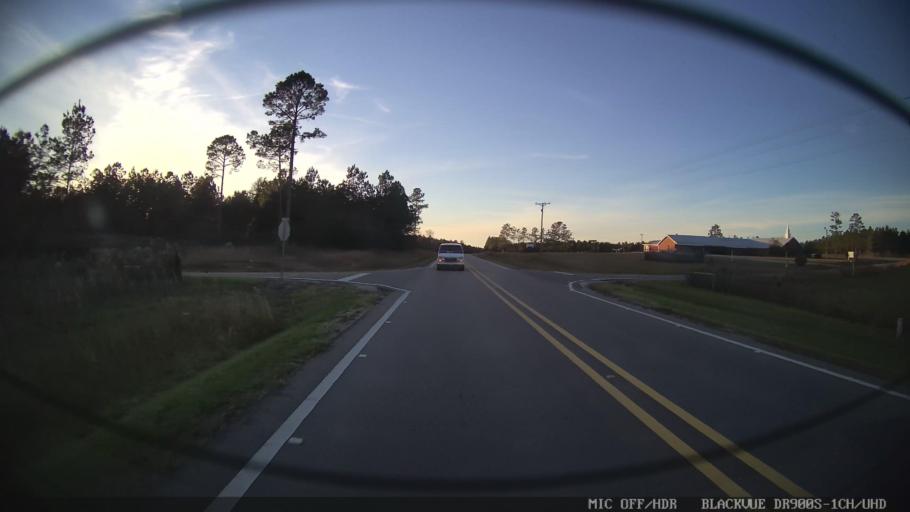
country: US
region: Mississippi
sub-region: Lamar County
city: Lumberton
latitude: 30.9924
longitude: -89.2816
